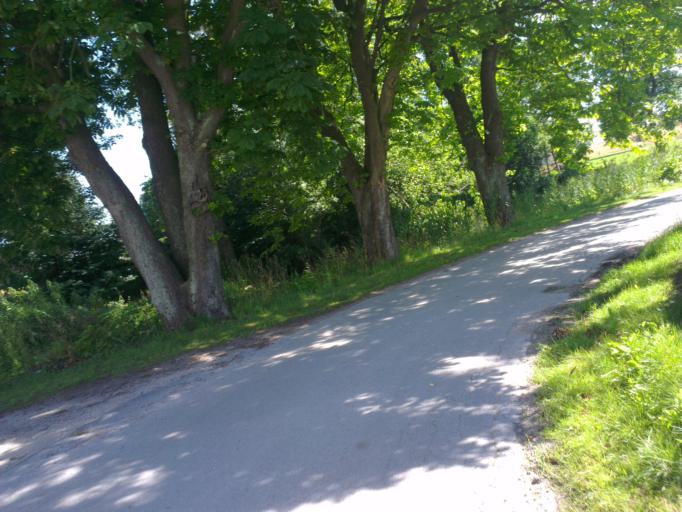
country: DK
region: Capital Region
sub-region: Frederikssund Kommune
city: Frederikssund
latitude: 55.8612
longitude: 12.1004
